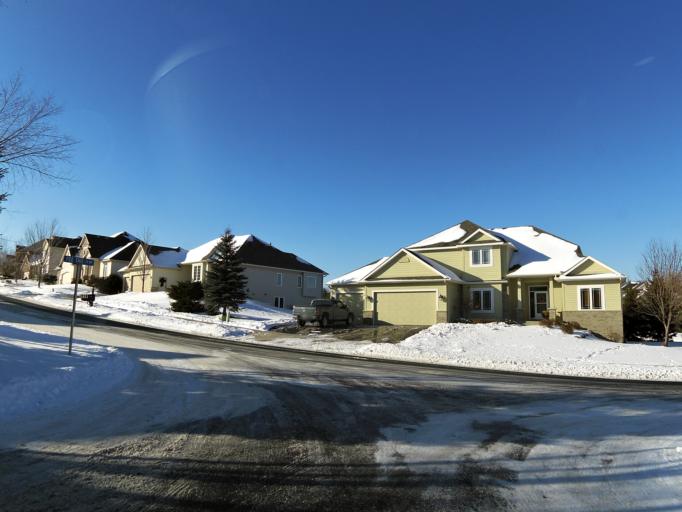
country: US
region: Minnesota
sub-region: Scott County
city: Prior Lake
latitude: 44.7280
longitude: -93.4550
